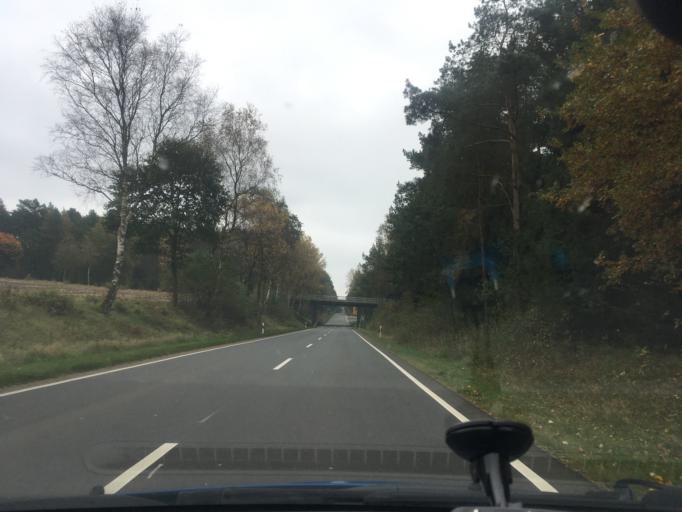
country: DE
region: Lower Saxony
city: Bispingen
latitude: 53.0728
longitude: 9.9701
